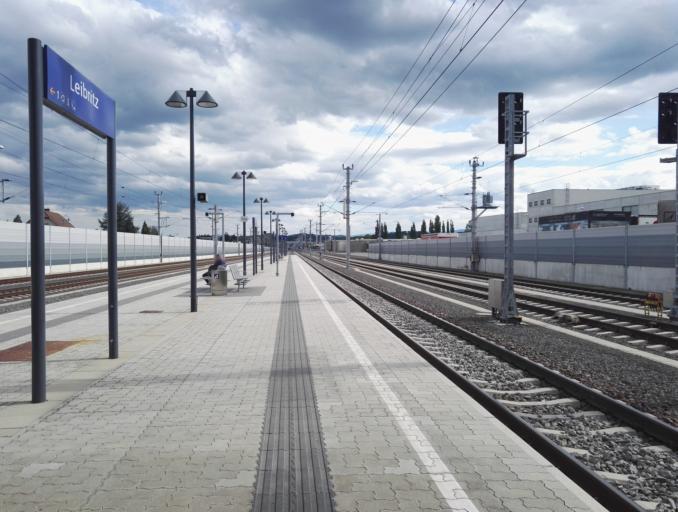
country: AT
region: Styria
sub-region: Politischer Bezirk Leibnitz
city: Leibnitz
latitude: 46.7794
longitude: 15.5475
